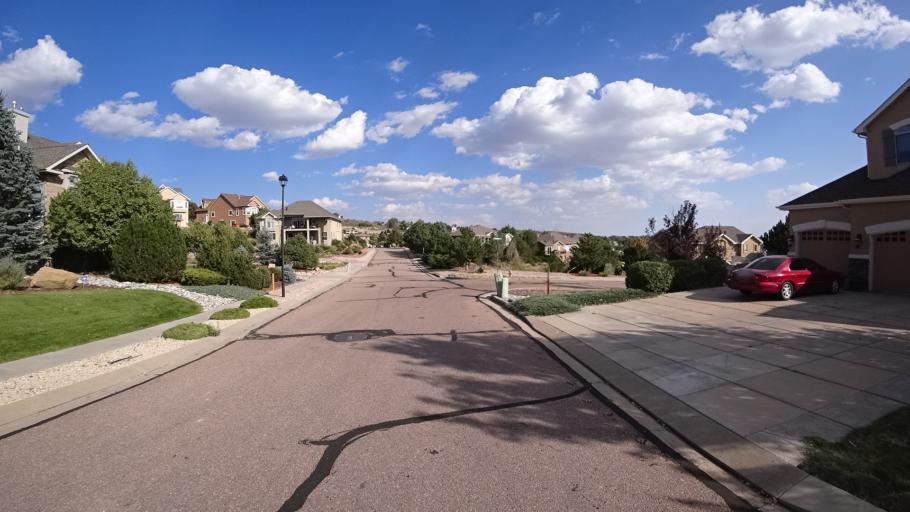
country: US
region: Colorado
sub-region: El Paso County
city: Cimarron Hills
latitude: 38.9109
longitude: -104.7380
